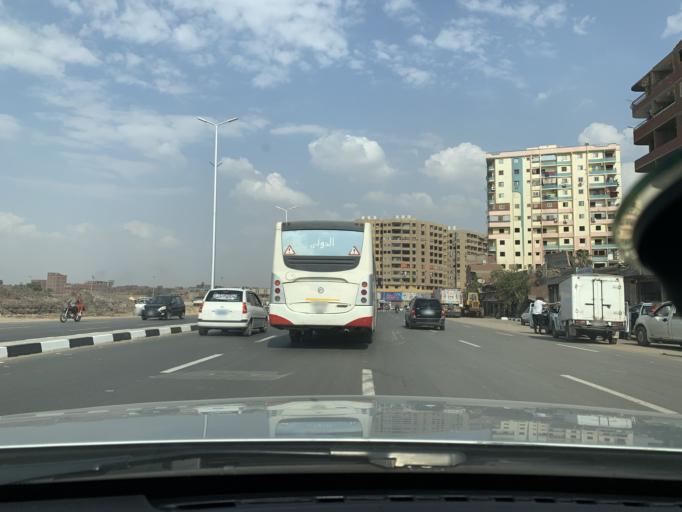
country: EG
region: Muhafazat al Qahirah
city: Cairo
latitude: 30.1292
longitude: 31.2942
